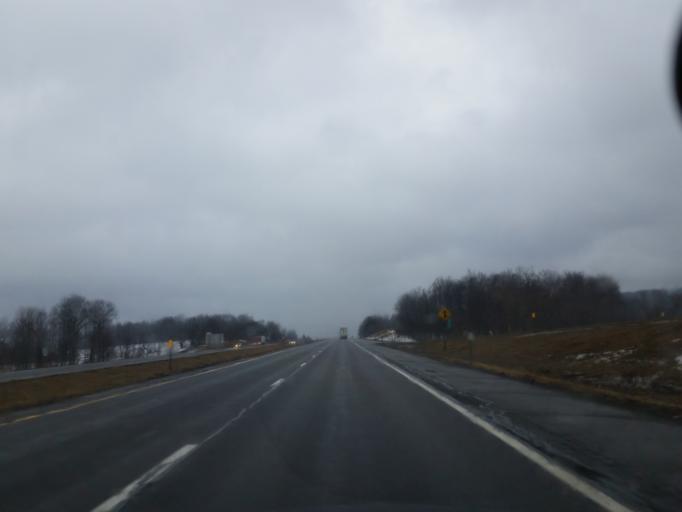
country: US
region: New York
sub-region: Chenango County
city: Lakeview
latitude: 42.3202
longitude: -75.9697
